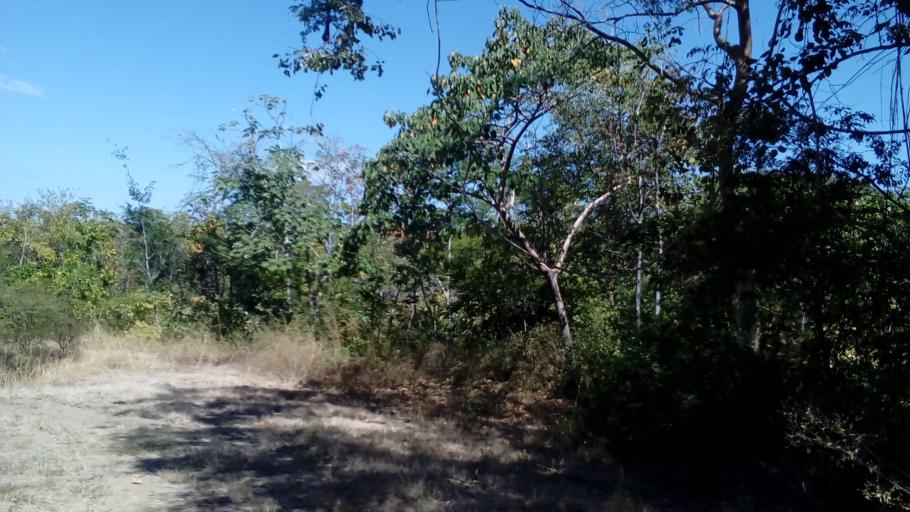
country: CR
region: Guanacaste
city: Sardinal
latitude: 10.3617
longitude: -85.8384
